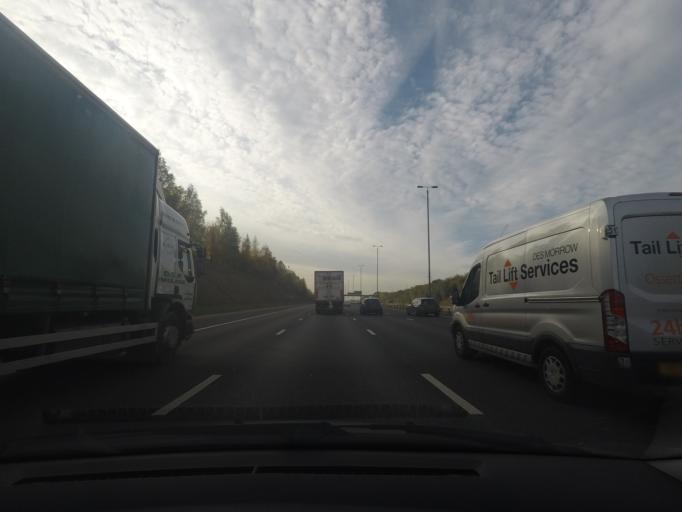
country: GB
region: England
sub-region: City and Borough of Leeds
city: Aberford
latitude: 53.8283
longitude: -1.3380
